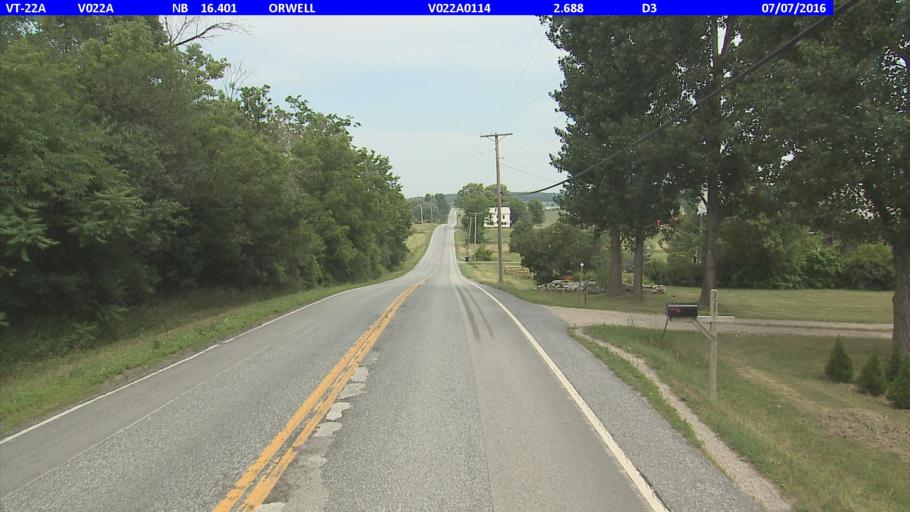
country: US
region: New York
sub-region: Essex County
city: Ticonderoga
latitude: 43.7958
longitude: -73.3062
